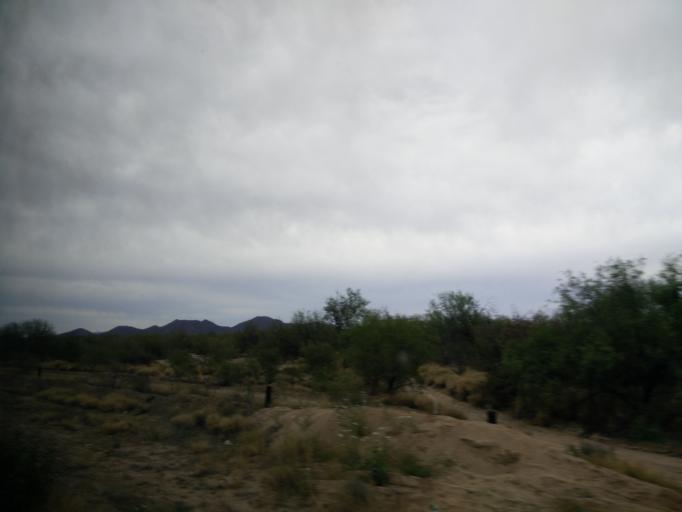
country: MX
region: Sonora
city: Hermosillo
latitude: 28.7474
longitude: -110.9736
